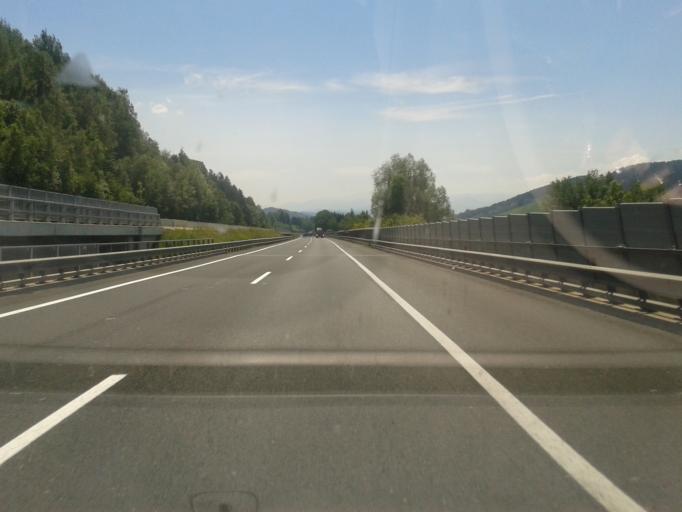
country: AT
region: Carinthia
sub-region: Politischer Bezirk Wolfsberg
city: Wolfsberg
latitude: 46.8773
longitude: 14.8316
